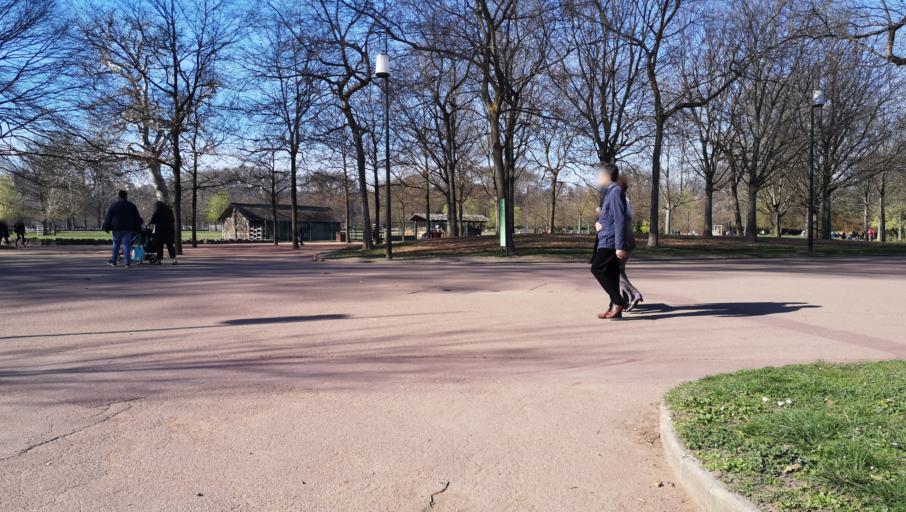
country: FR
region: Rhone-Alpes
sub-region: Departement du Rhone
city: Caluire-et-Cuire
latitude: 45.7737
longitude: 4.8546
